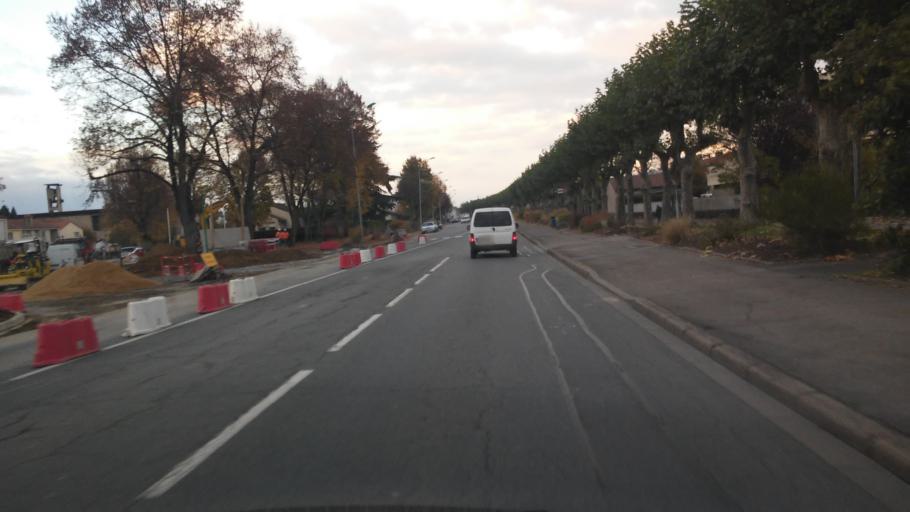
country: FR
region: Lorraine
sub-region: Departement de la Moselle
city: Maizieres-les-Metz
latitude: 49.2055
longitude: 6.1611
